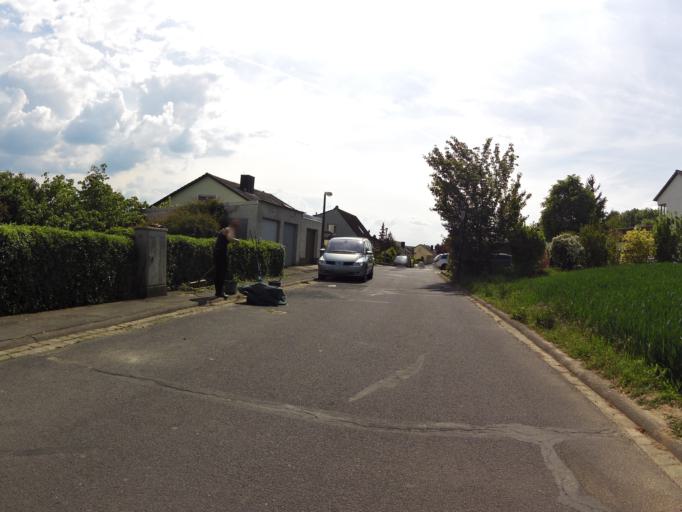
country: DE
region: Bavaria
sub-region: Regierungsbezirk Unterfranken
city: Theilheim
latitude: 49.7355
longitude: 10.0318
